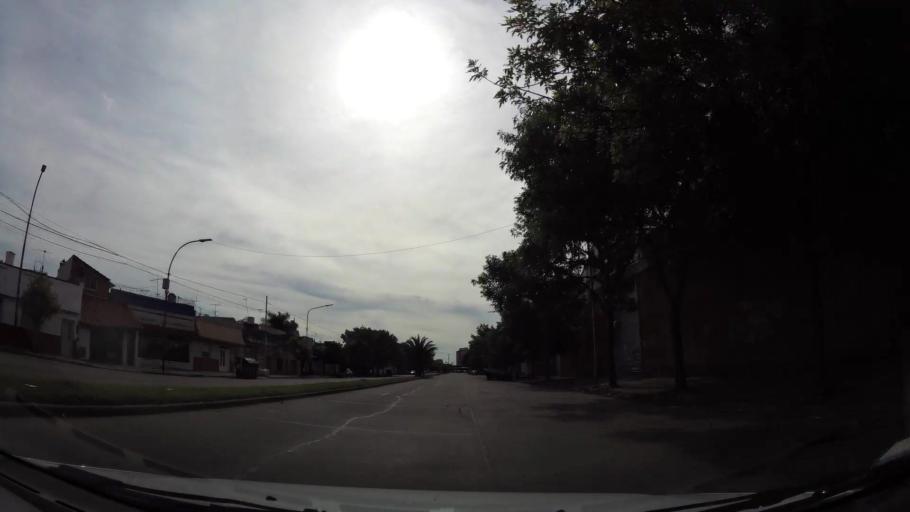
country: AR
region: Buenos Aires F.D.
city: Villa Lugano
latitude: -34.6541
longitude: -58.4784
